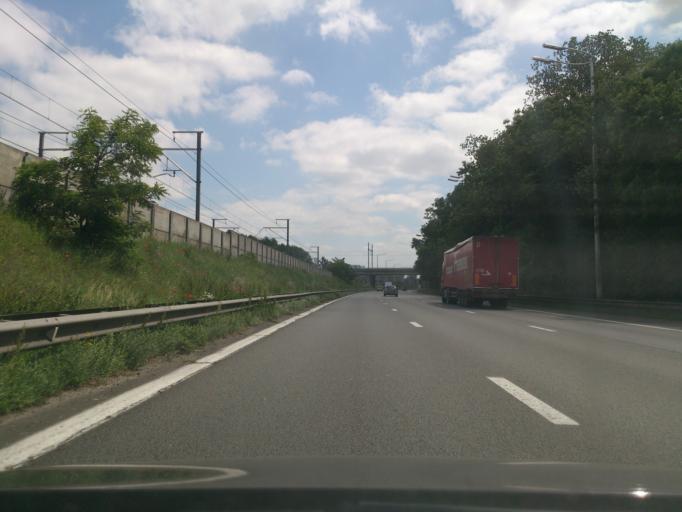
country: BE
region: Flanders
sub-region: Provincie Vlaams-Brabant
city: Zemst
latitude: 50.9847
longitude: 4.4811
